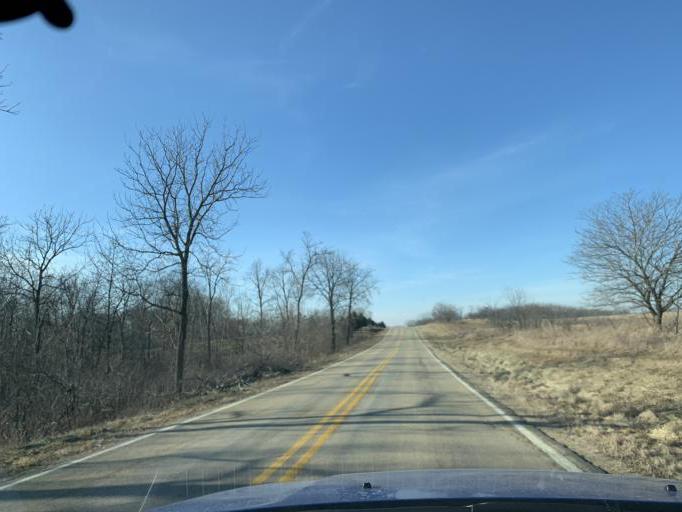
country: US
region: Wisconsin
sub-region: Iowa County
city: Barneveld
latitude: 42.8135
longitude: -89.9029
